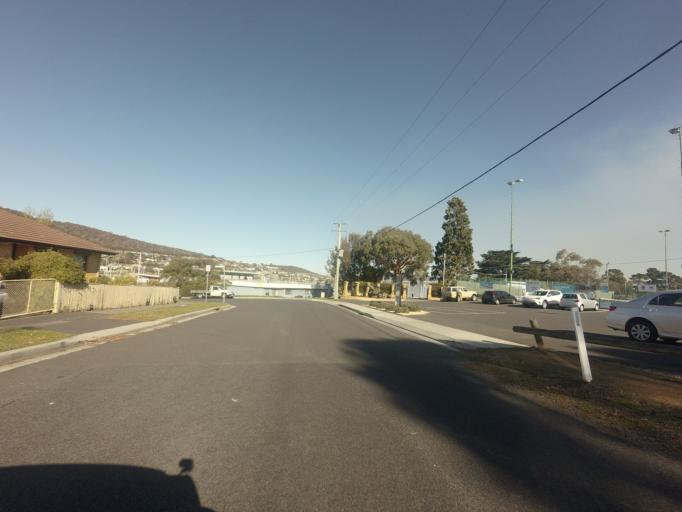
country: AU
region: Tasmania
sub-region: Clarence
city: Lindisfarne
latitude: -42.8507
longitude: 147.3521
